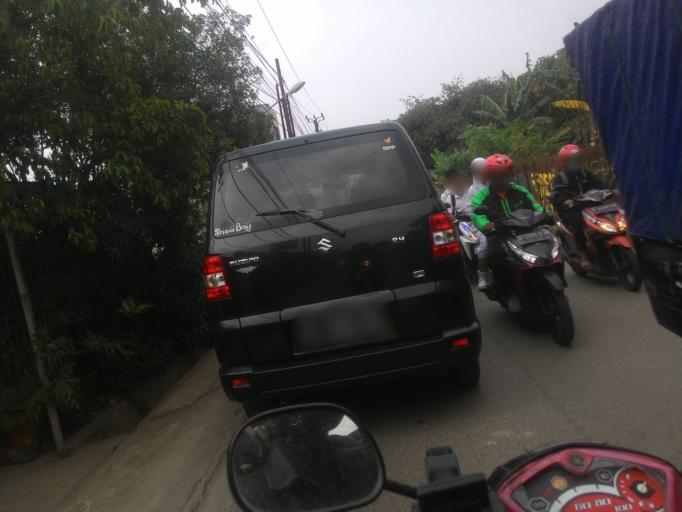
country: ID
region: West Java
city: Depok
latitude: -6.4187
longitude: 106.8411
